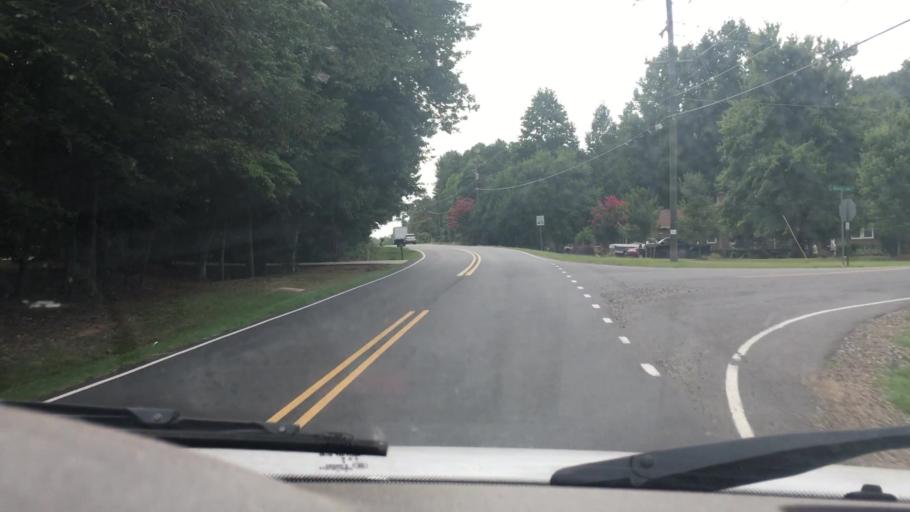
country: US
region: North Carolina
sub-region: Gaston County
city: Davidson
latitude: 35.5383
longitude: -80.8343
